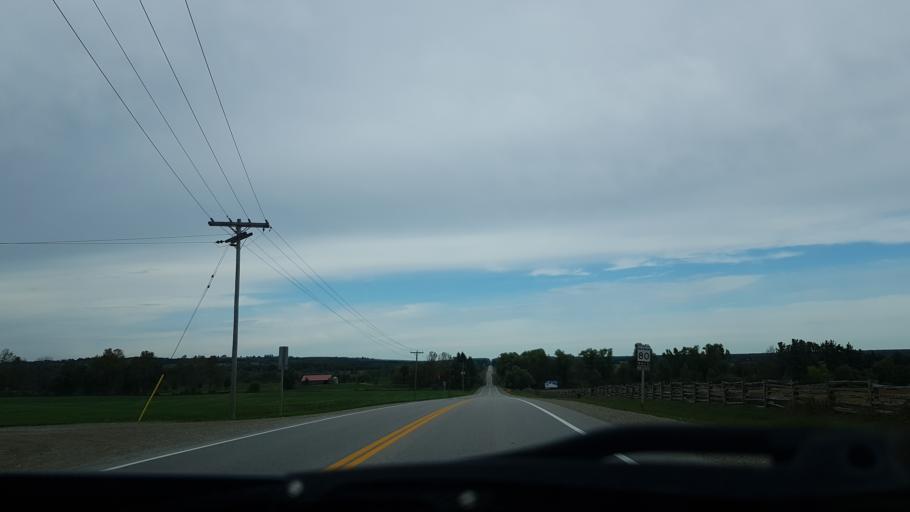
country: CA
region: Ontario
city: Shelburne
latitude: 44.1446
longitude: -80.0322
